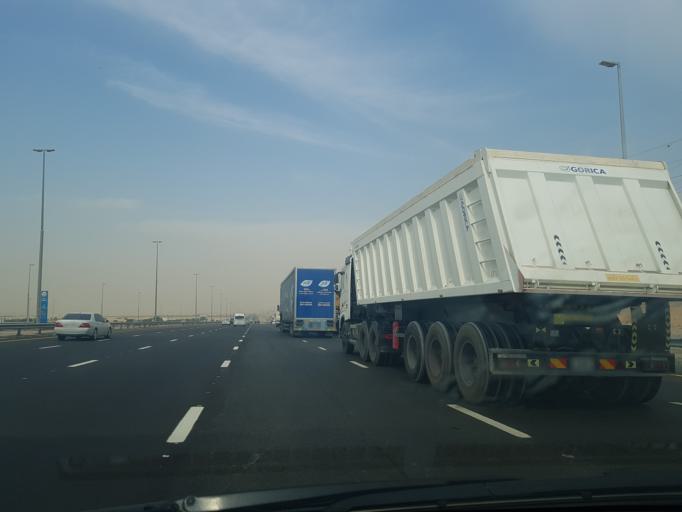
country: AE
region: Ash Shariqah
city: Sharjah
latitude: 25.2551
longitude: 55.5744
